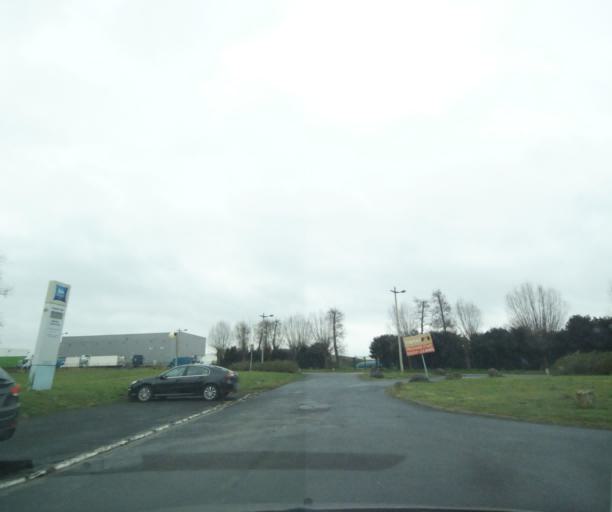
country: FR
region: Nord-Pas-de-Calais
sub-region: Departement du Nord
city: Herin
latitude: 50.3367
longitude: 3.4570
